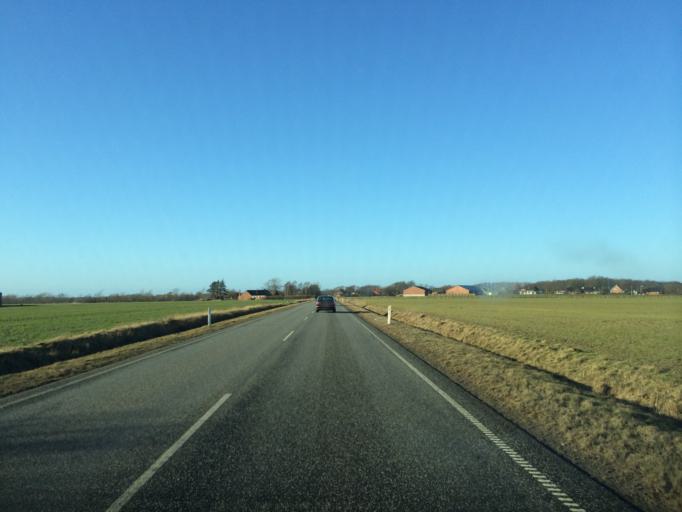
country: DK
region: Central Jutland
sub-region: Ringkobing-Skjern Kommune
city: Ringkobing
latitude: 56.1056
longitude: 8.3240
